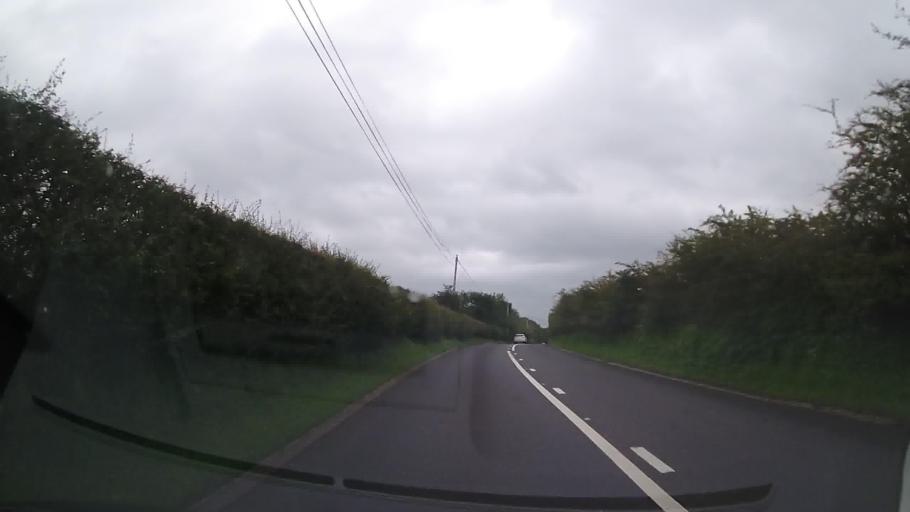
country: GB
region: England
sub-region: Staffordshire
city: Newcastle under Lyme
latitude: 52.9736
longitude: -2.2612
